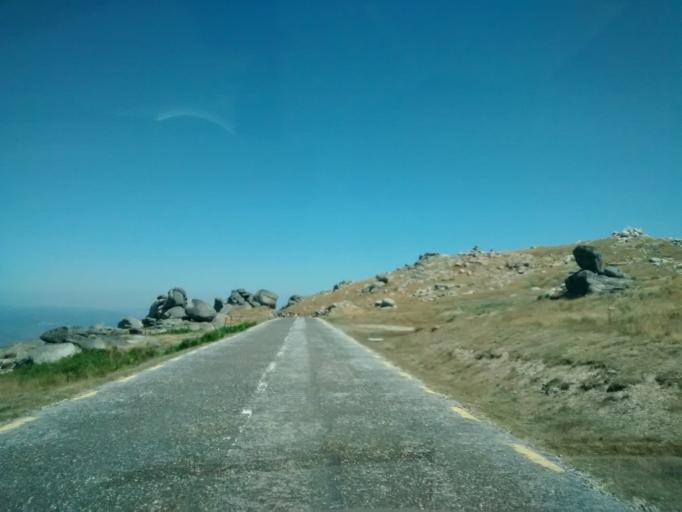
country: PT
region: Guarda
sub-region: Seia
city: Seia
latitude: 40.4209
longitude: -7.6272
